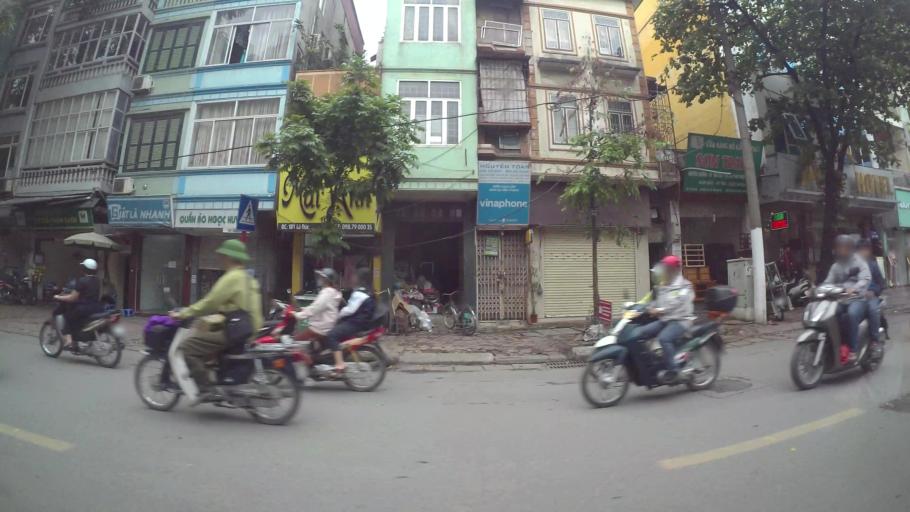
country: VN
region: Ha Noi
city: Hai BaTrung
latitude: 21.0099
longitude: 105.8606
